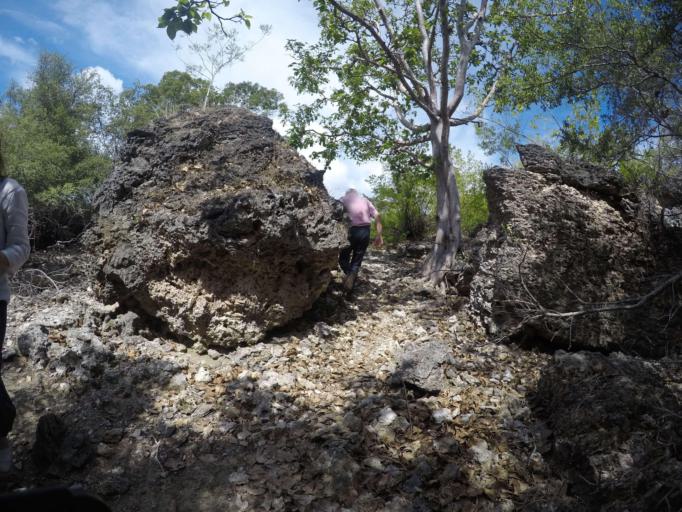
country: TL
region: Lautem
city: Lospalos
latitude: -8.3459
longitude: 127.0485
